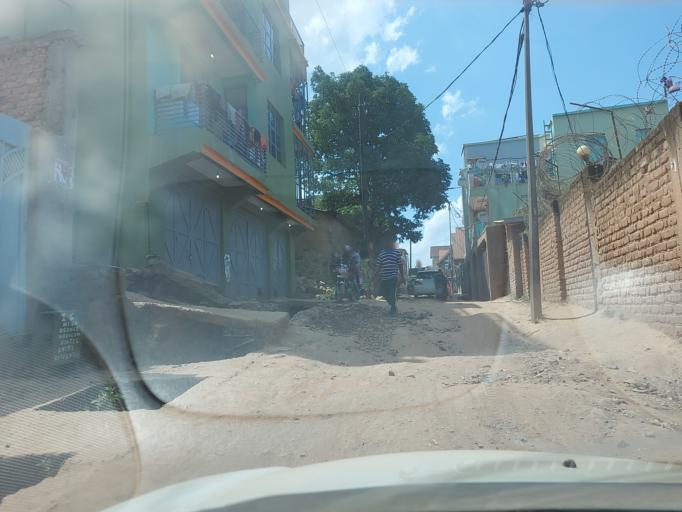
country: CD
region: South Kivu
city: Bukavu
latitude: -2.5014
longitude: 28.8751
